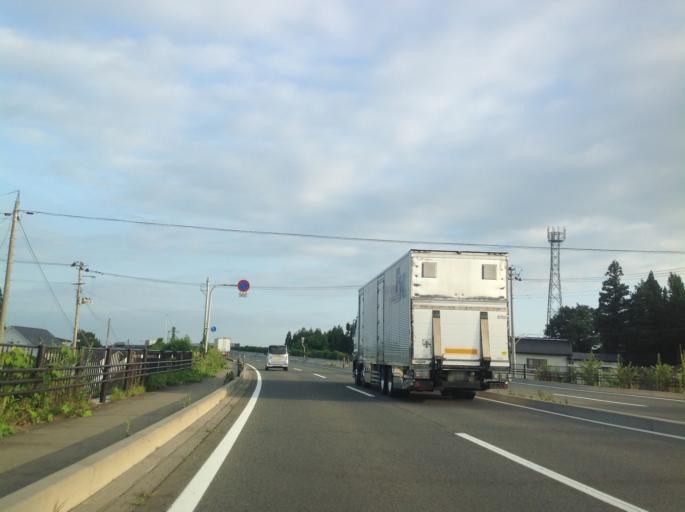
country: JP
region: Iwate
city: Hanamaki
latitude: 39.4747
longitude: 141.1391
